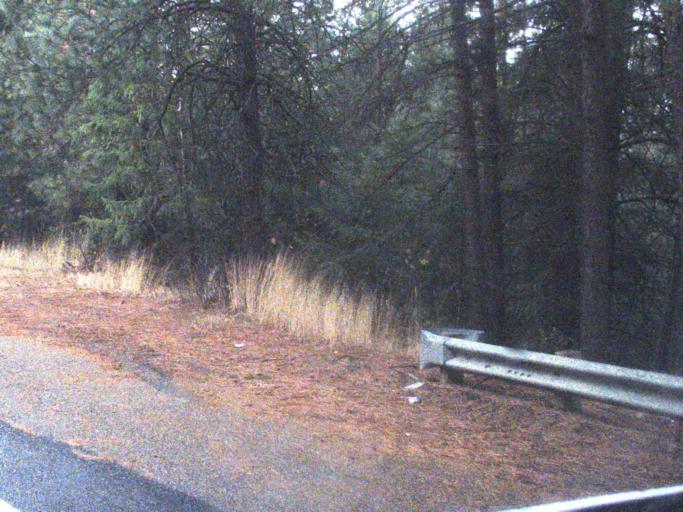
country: US
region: Washington
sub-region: Stevens County
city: Kettle Falls
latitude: 48.5706
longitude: -118.1020
